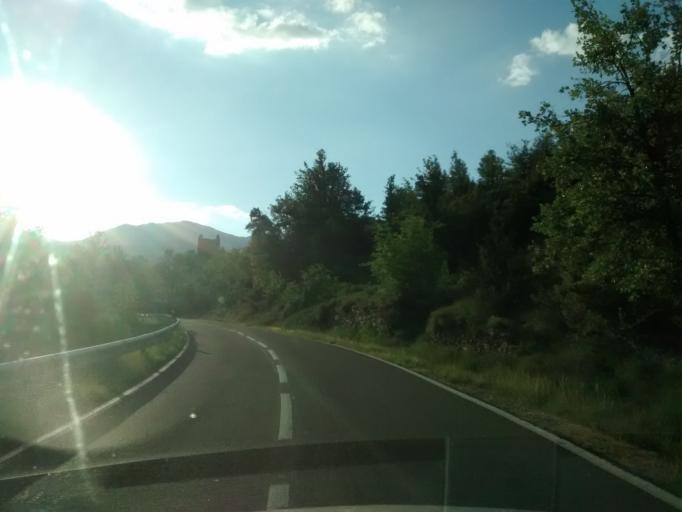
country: ES
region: Aragon
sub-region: Provincia de Huesca
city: Boltana
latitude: 42.4727
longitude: -0.0028
